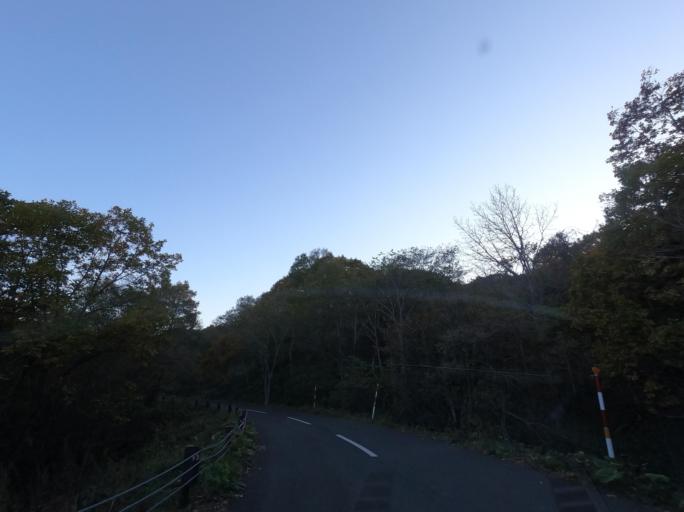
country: JP
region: Hokkaido
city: Kushiro
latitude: 43.2030
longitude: 144.4567
